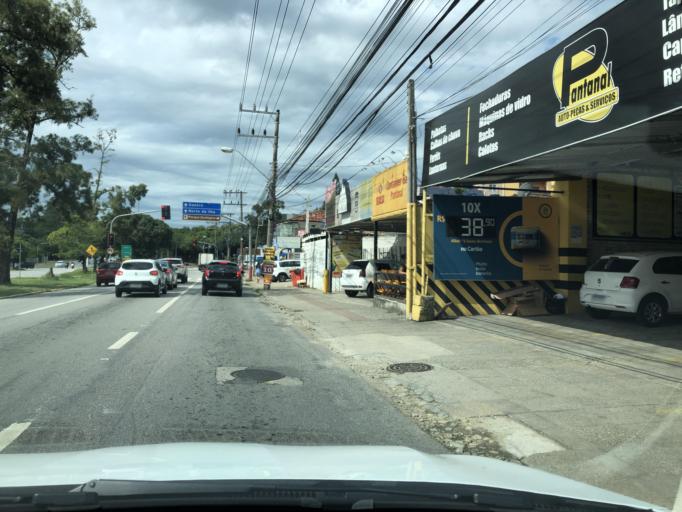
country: BR
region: Santa Catarina
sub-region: Florianopolis
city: Pantanal
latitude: -27.6012
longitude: -48.5169
